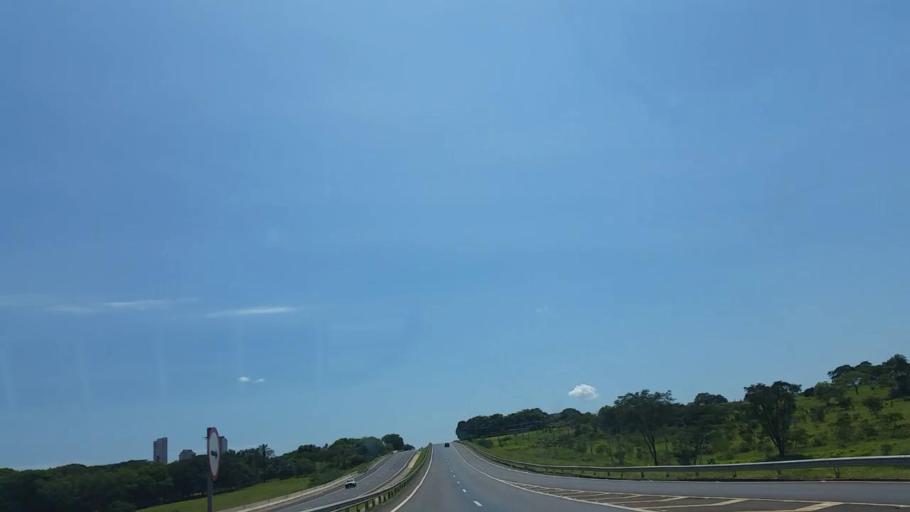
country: BR
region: Sao Paulo
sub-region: Bauru
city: Bauru
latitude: -22.3846
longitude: -49.0699
